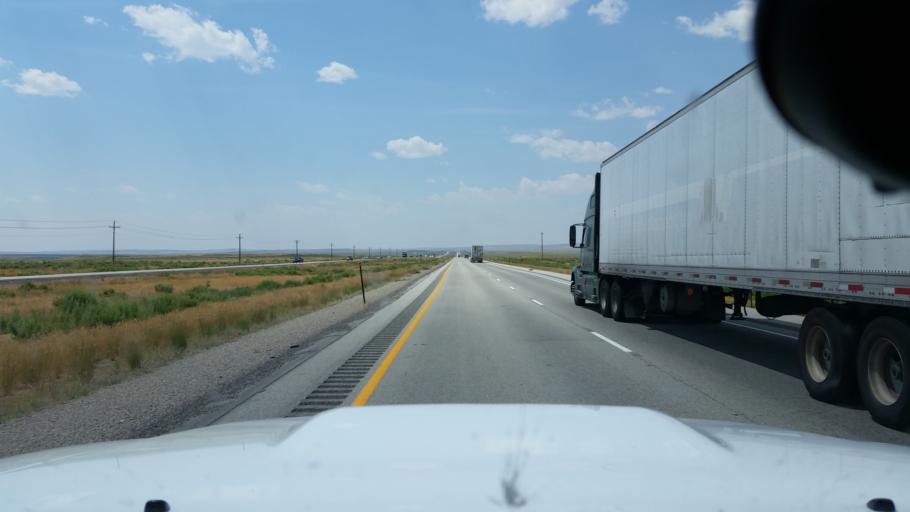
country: US
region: Wyoming
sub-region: Carbon County
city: Rawlins
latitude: 41.7820
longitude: -107.4271
